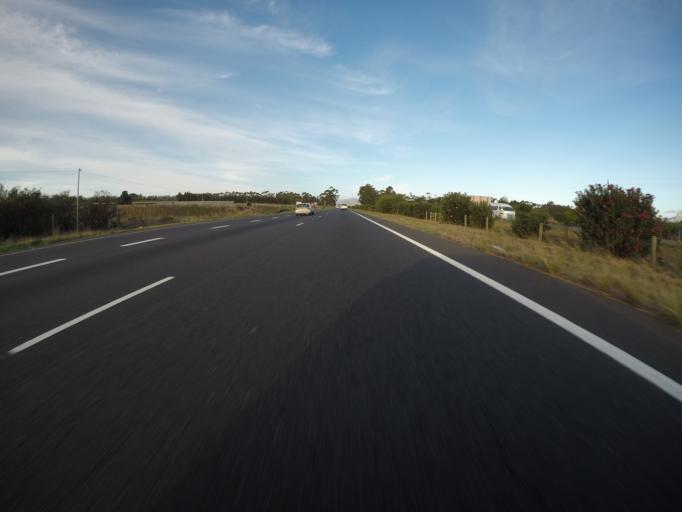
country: ZA
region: Western Cape
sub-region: Cape Winelands District Municipality
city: Paarl
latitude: -33.7977
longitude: 18.8754
